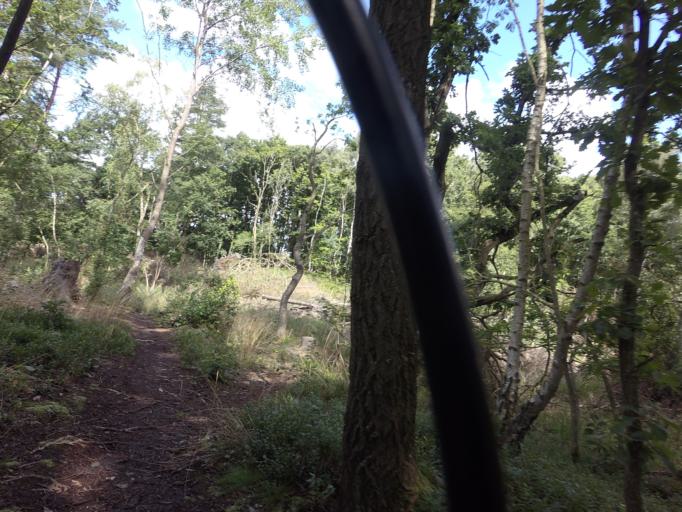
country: DK
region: Central Jutland
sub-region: Silkeborg Kommune
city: Svejbaek
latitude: 56.2182
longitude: 9.6884
